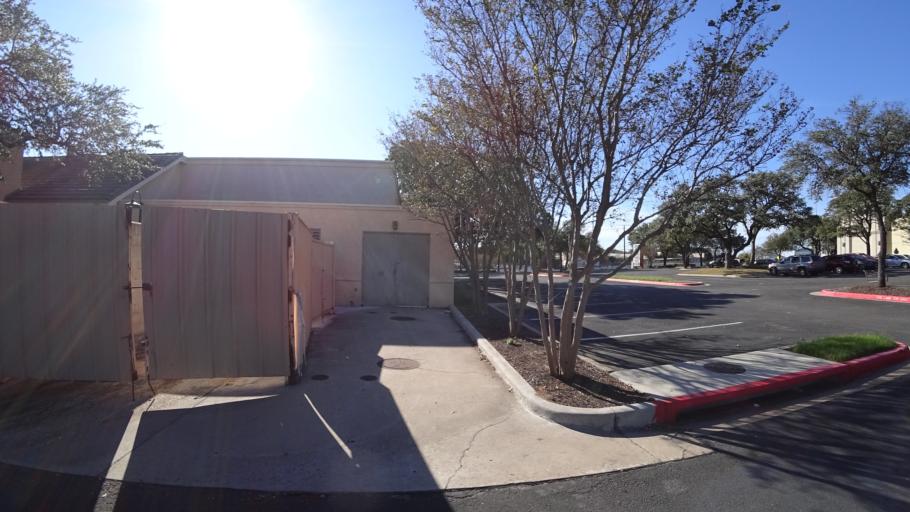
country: US
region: Texas
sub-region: Williamson County
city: Jollyville
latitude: 30.3862
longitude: -97.7414
